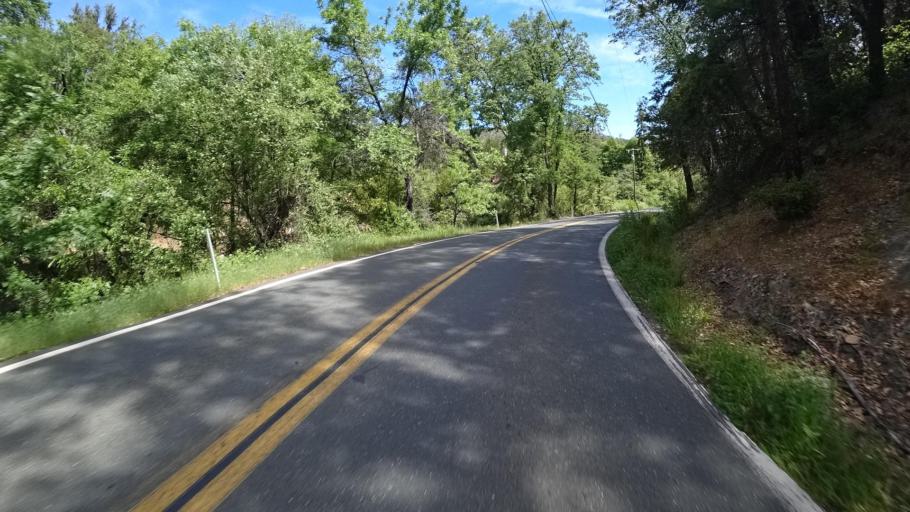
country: US
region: California
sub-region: Lake County
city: Cobb
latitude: 38.8786
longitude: -122.6763
